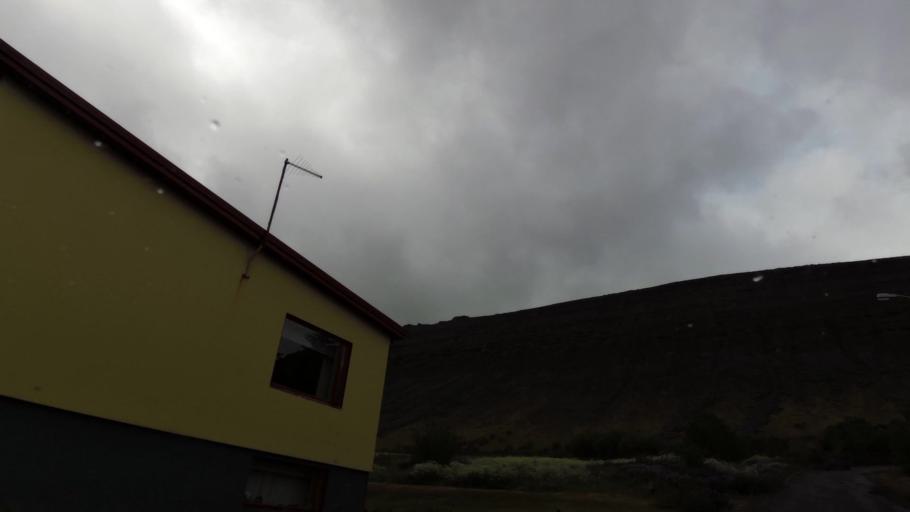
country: IS
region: Westfjords
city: Isafjoerdur
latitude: 65.8734
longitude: -23.4863
